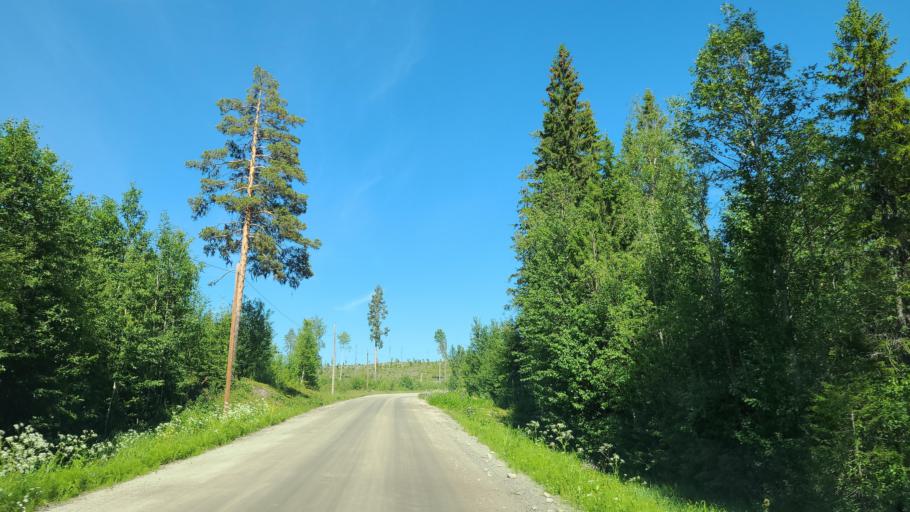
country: SE
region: Vaesterbotten
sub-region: Bjurholms Kommun
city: Bjurholm
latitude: 63.7045
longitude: 18.9030
